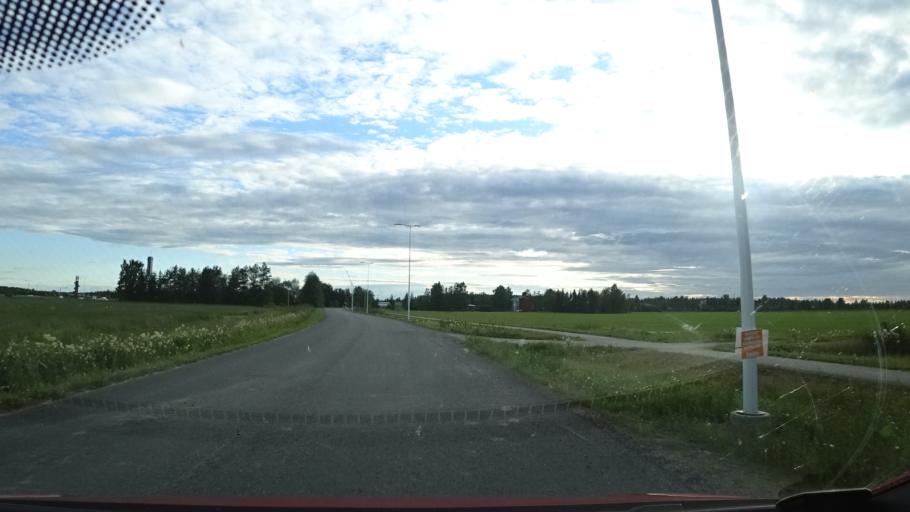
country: FI
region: Northern Ostrobothnia
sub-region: Oulu
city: Liminka
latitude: 64.8098
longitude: 25.4632
